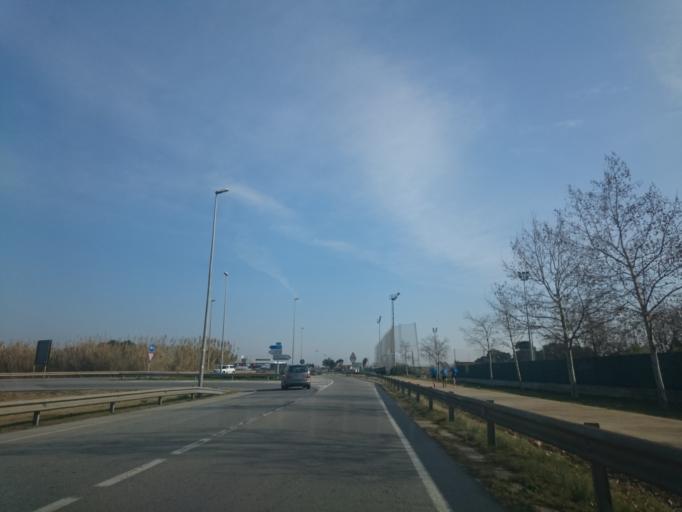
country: ES
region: Catalonia
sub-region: Provincia de Barcelona
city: Gava
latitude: 41.2899
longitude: 2.0118
